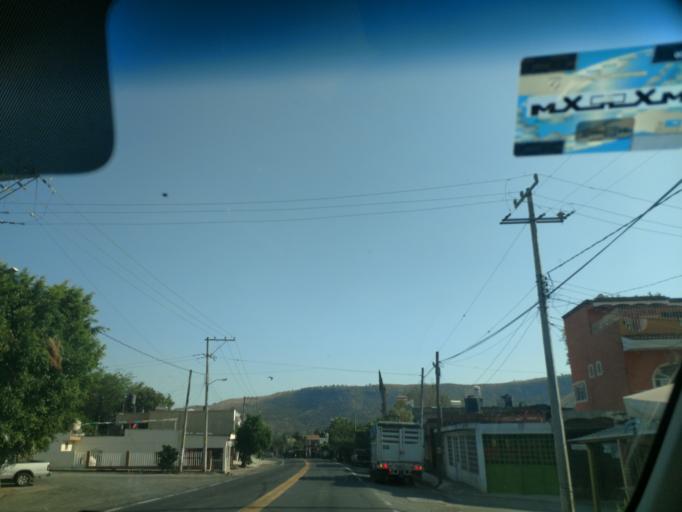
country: MX
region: Nayarit
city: San Pedro Lagunillas
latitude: 21.1620
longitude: -104.6244
